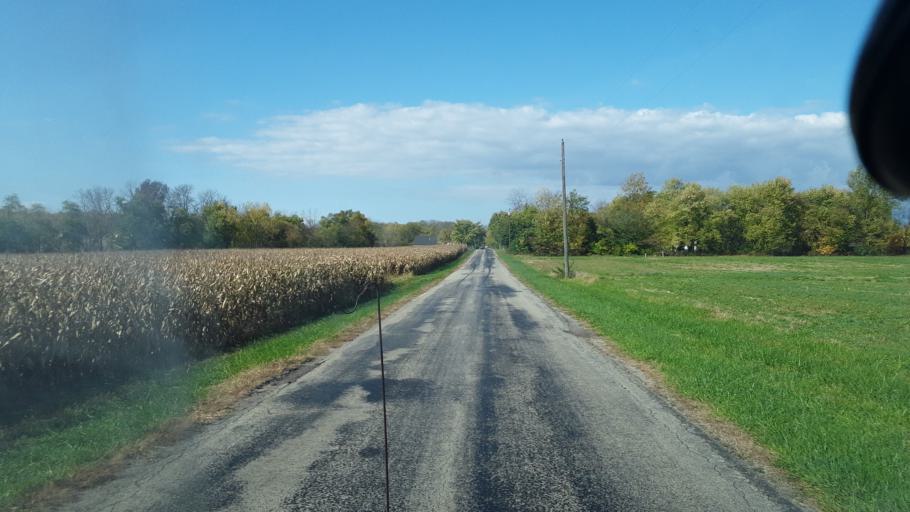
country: US
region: Ohio
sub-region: Highland County
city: Leesburg
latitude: 39.2831
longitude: -83.5876
